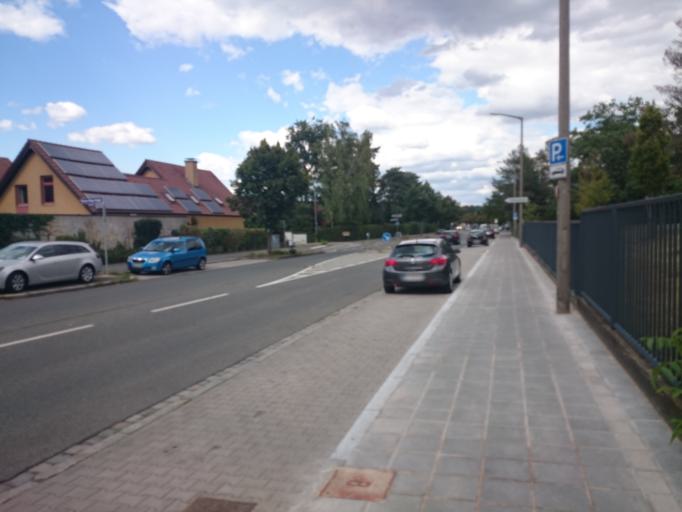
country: DE
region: Bavaria
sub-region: Regierungsbezirk Mittelfranken
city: Wendelstein
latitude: 49.4110
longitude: 11.1318
